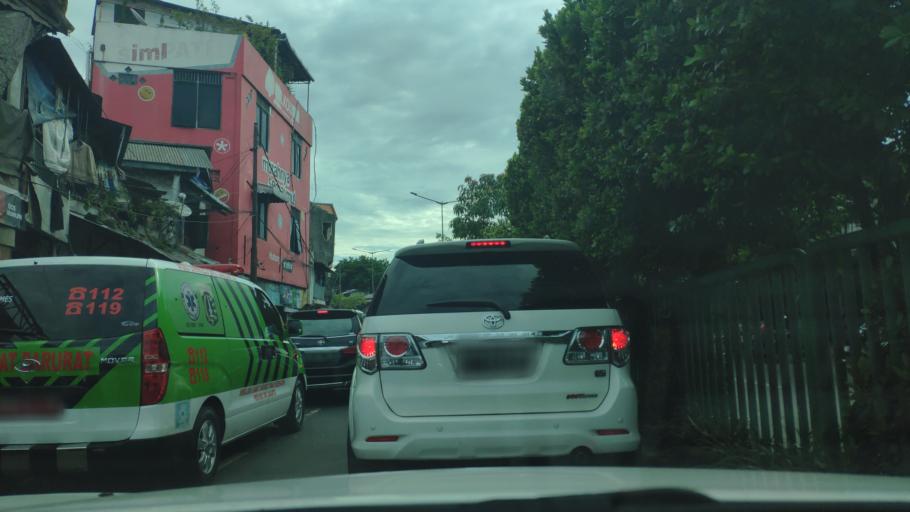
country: ID
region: Jakarta Raya
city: Jakarta
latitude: -6.1874
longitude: 106.8073
